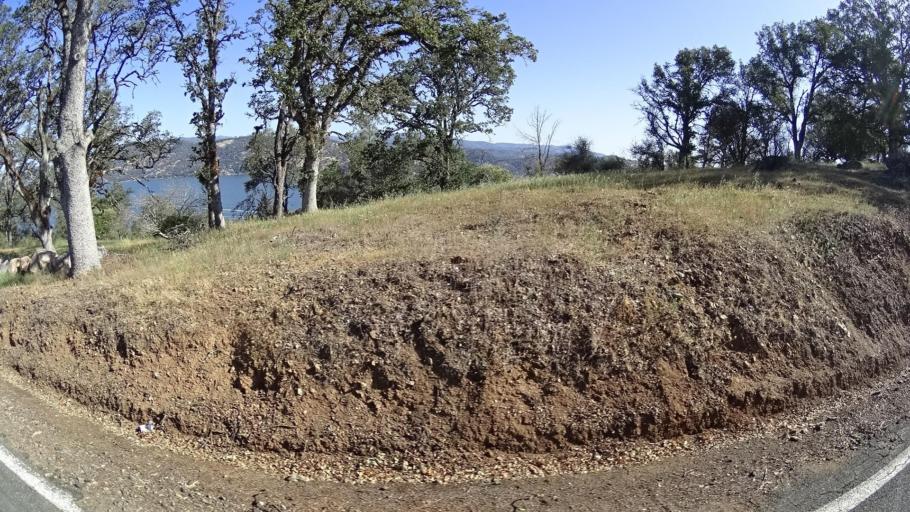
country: US
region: California
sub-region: Lake County
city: Clearlake Oaks
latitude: 38.9946
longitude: -122.6774
